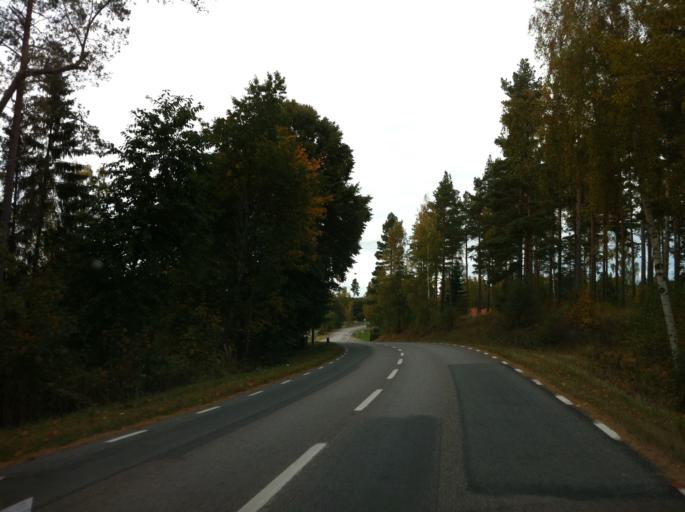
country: SE
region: OEstergoetland
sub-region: Motala Kommun
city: Motala
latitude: 58.6209
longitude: 14.9724
